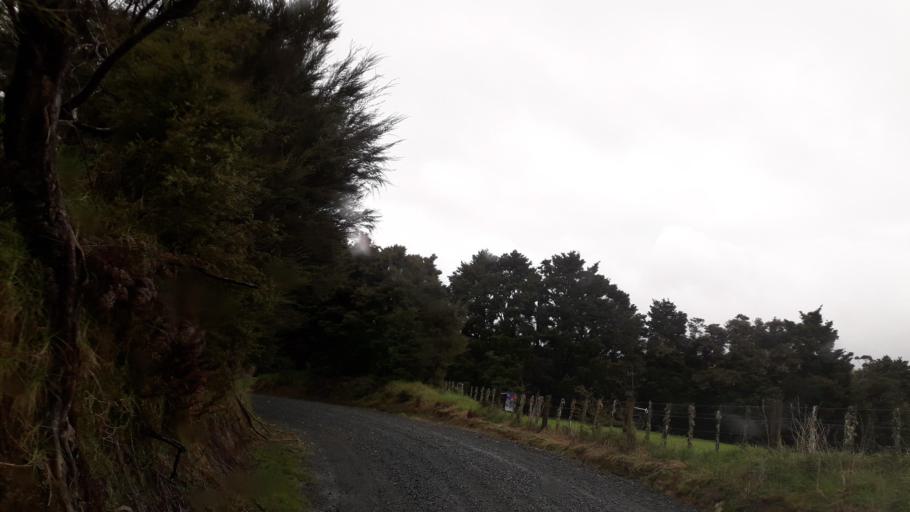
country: NZ
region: Northland
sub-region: Far North District
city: Waimate North
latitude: -35.1507
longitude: 173.7119
